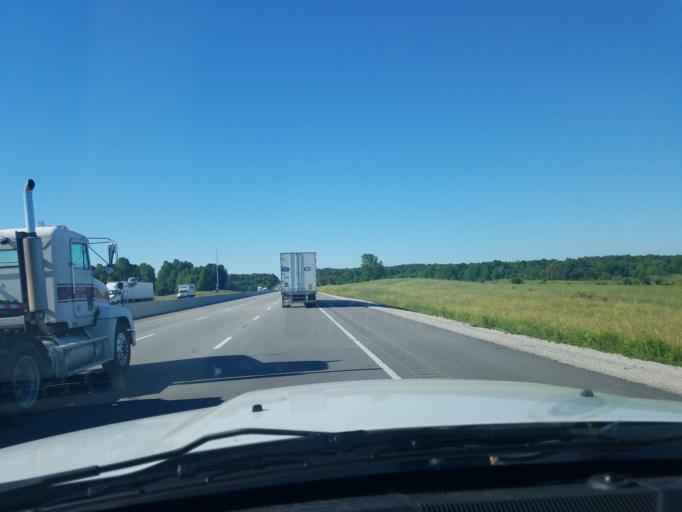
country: US
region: Kentucky
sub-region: Larue County
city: Hodgenville
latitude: 37.4841
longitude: -85.8810
